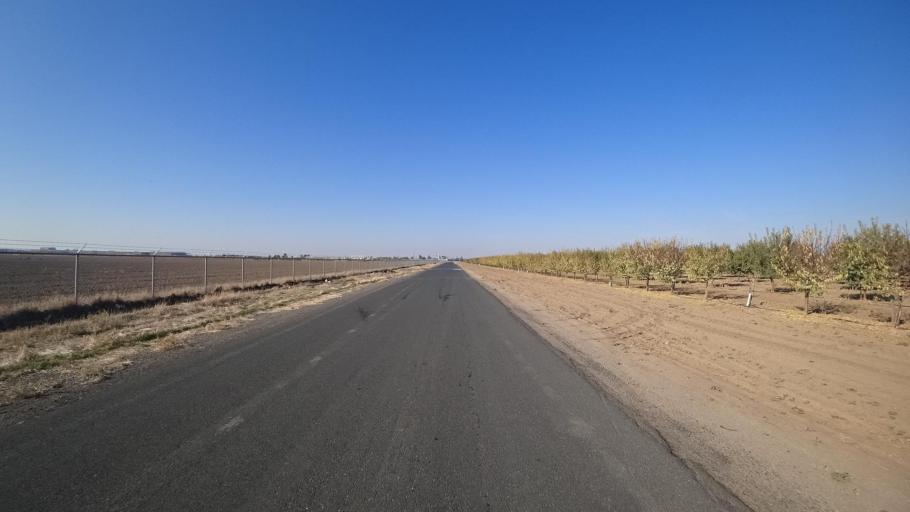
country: US
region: California
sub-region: Kern County
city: Delano
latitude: 35.7469
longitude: -119.2281
